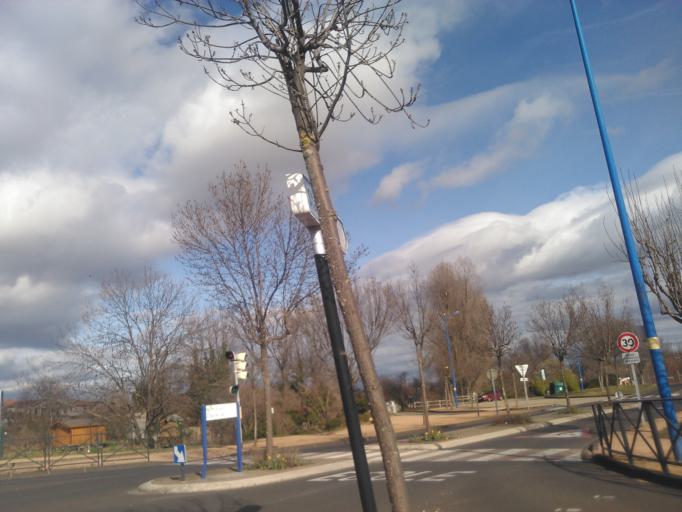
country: FR
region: Auvergne
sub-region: Departement du Puy-de-Dome
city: Aubiere
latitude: 45.7520
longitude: 3.1182
